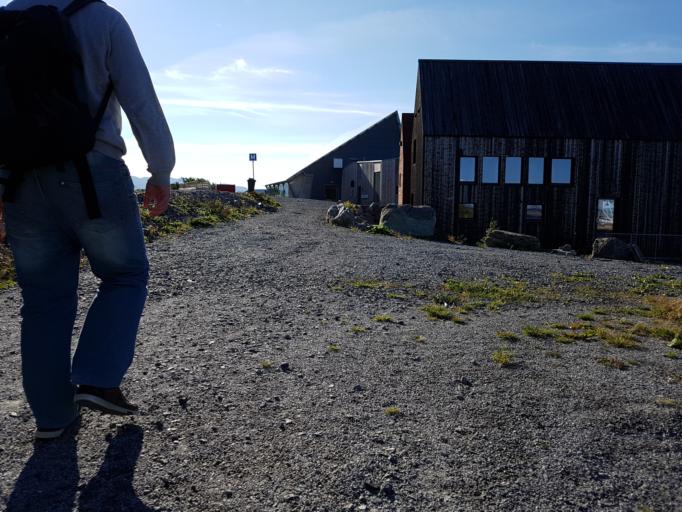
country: NO
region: Sor-Trondelag
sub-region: Afjord
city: A i Afjord
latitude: 64.0469
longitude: 9.9460
